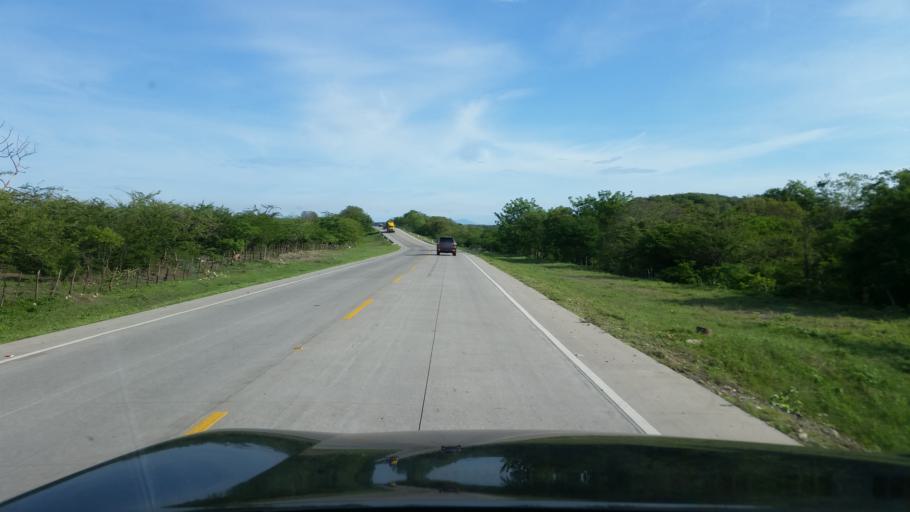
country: NI
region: Leon
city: Nagarote
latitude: 12.1758
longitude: -86.6672
